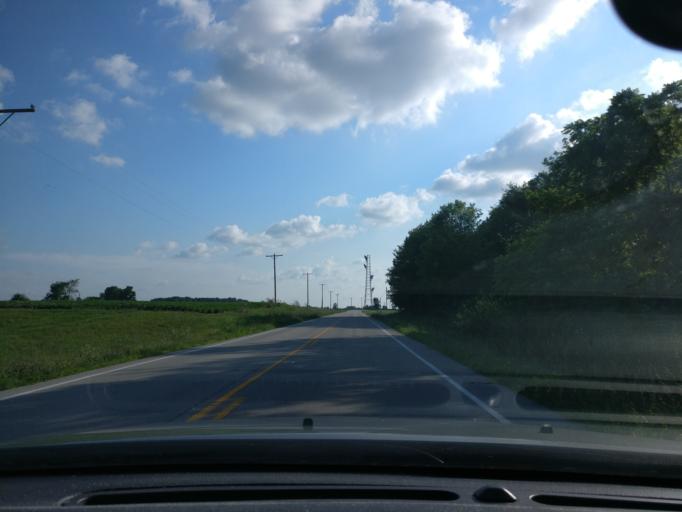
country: US
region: Ohio
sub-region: Clinton County
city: Wilmington
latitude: 39.5433
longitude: -83.7986
